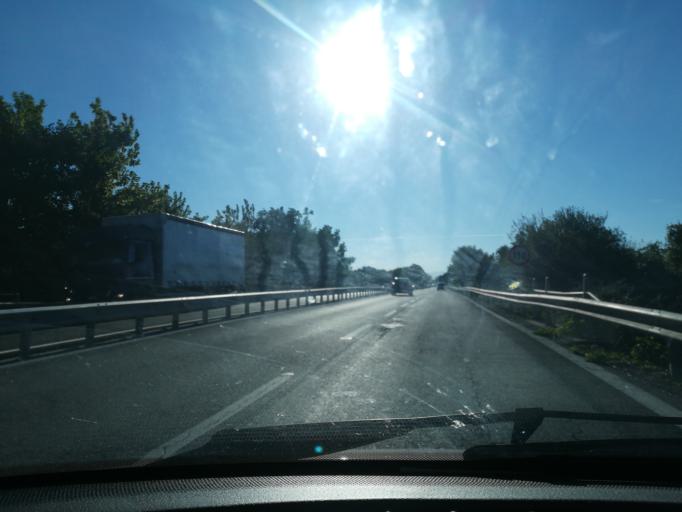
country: IT
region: The Marches
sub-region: Provincia di Macerata
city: Zona Industriale
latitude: 43.2577
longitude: 13.4604
